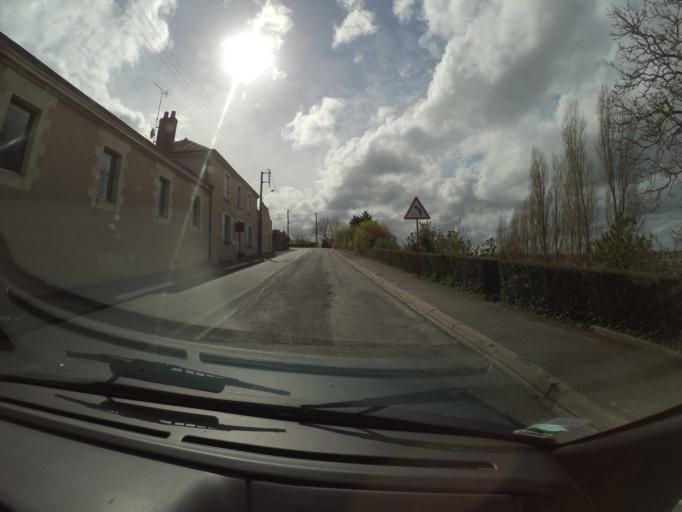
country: FR
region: Pays de la Loire
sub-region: Departement de Maine-et-Loire
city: Lire
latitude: 47.3442
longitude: -1.1646
